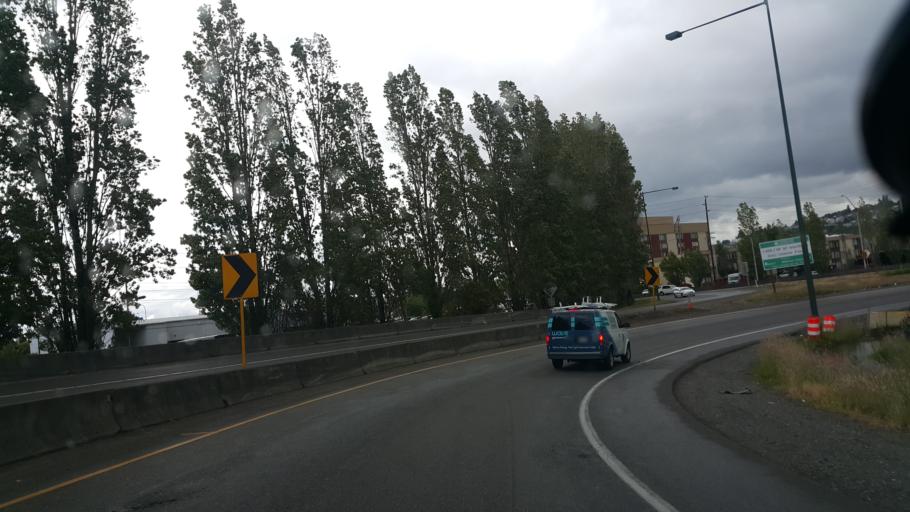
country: US
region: Washington
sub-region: King County
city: Renton
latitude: 47.4688
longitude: -122.2196
